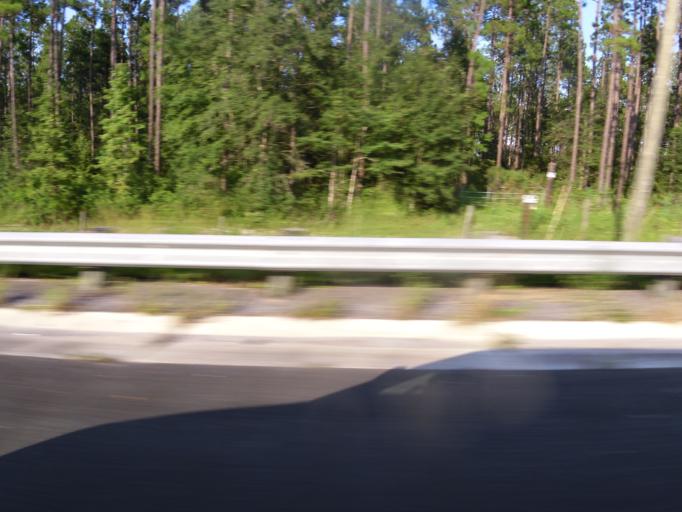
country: US
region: Florida
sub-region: Duval County
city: Baldwin
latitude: 30.3670
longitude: -82.0140
